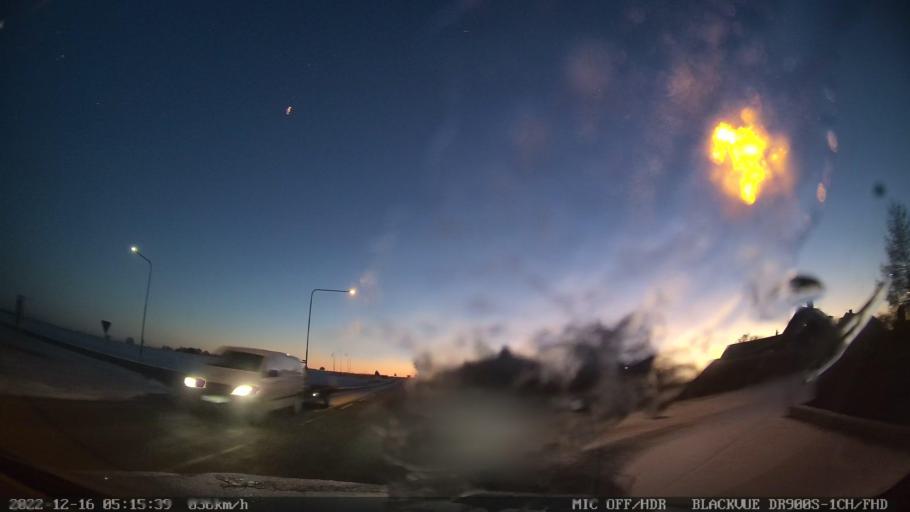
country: SE
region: Skane
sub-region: Tomelilla Kommun
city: Tomelilla
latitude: 55.5340
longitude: 13.9400
